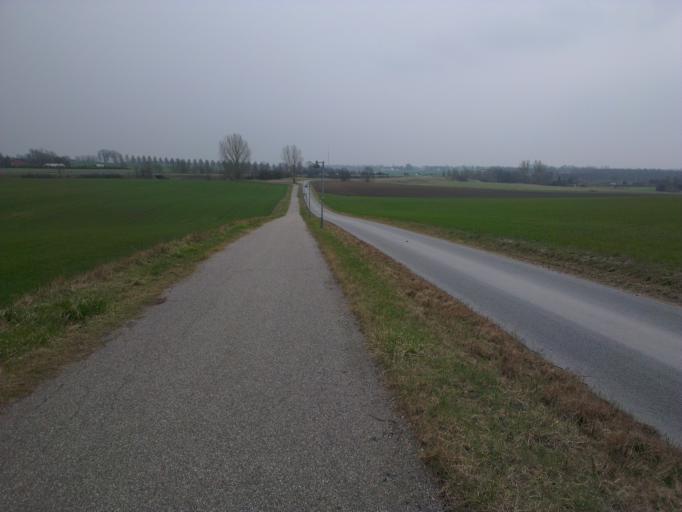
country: DK
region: Capital Region
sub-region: Frederikssund Kommune
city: Frederikssund
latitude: 55.8181
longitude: 12.1005
